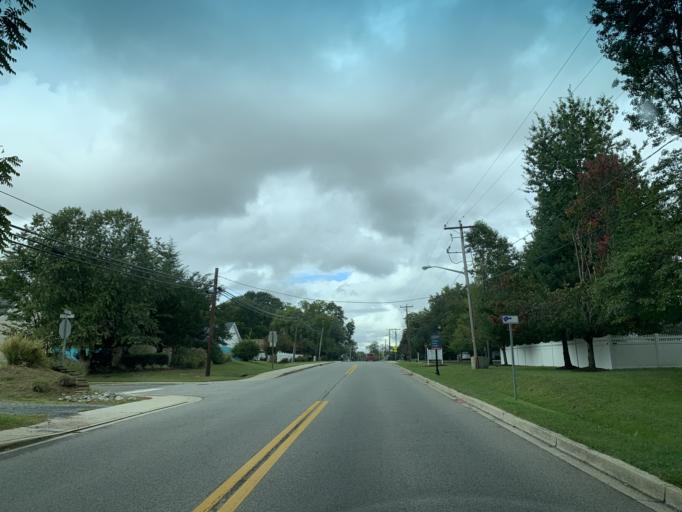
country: US
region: Maryland
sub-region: Caroline County
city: Denton
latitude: 38.8758
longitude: -75.8270
